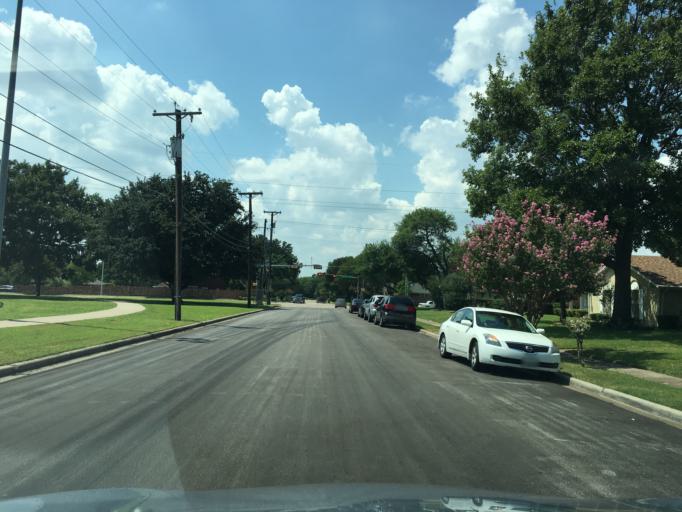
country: US
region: Texas
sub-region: Dallas County
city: Garland
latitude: 32.9388
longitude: -96.6640
